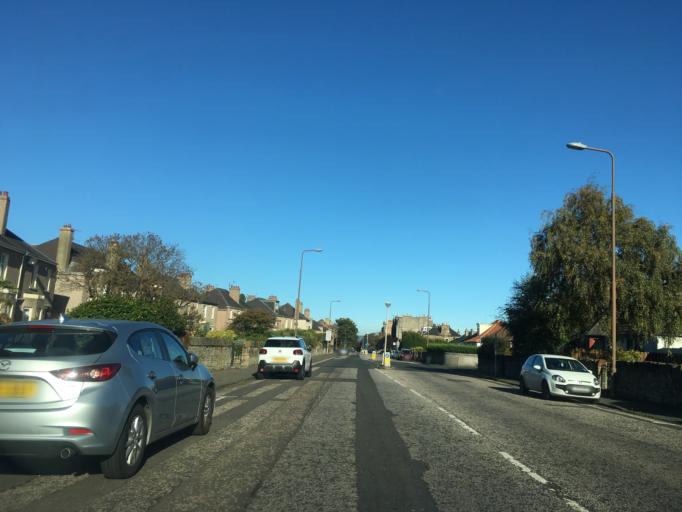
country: GB
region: Scotland
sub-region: Edinburgh
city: Edinburgh
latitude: 55.9734
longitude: -3.2150
